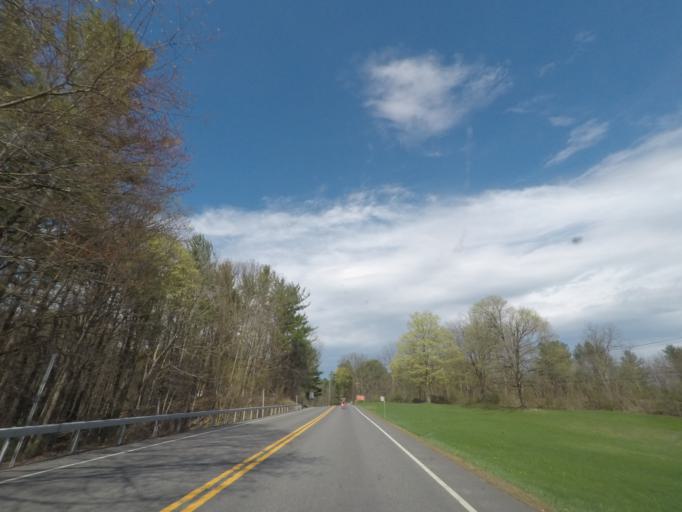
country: US
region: New York
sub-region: Greene County
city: Cairo
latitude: 42.3621
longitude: -74.0452
